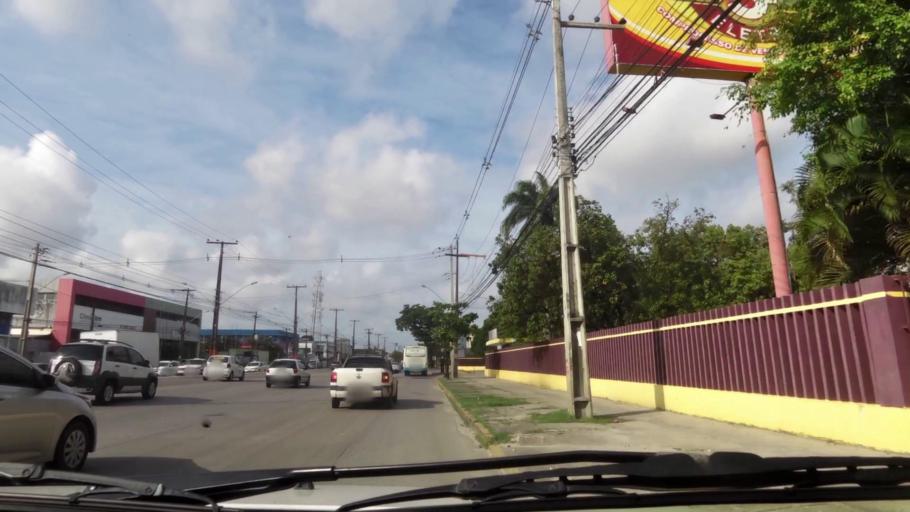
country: BR
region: Pernambuco
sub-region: Recife
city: Recife
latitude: -8.0950
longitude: -34.9093
